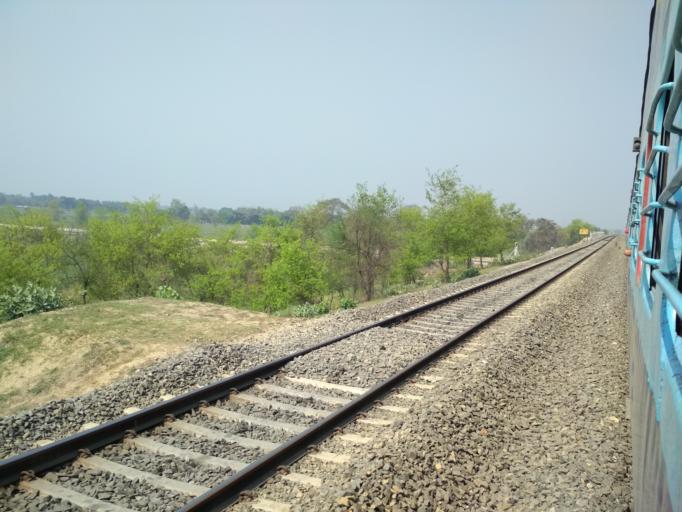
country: IN
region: Bihar
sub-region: Munger
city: Munger
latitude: 25.4369
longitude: 86.4345
